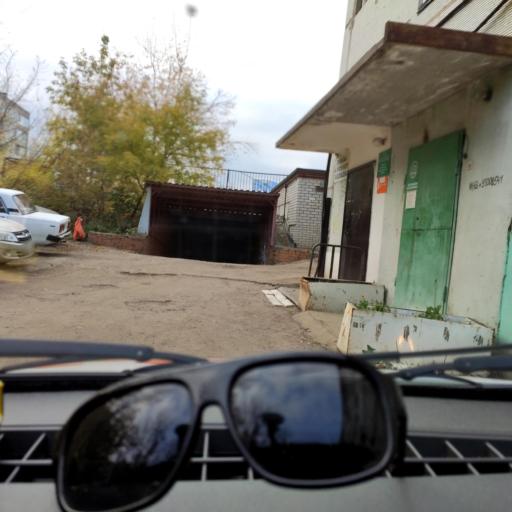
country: RU
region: Bashkortostan
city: Ufa
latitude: 54.7859
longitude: 56.0464
